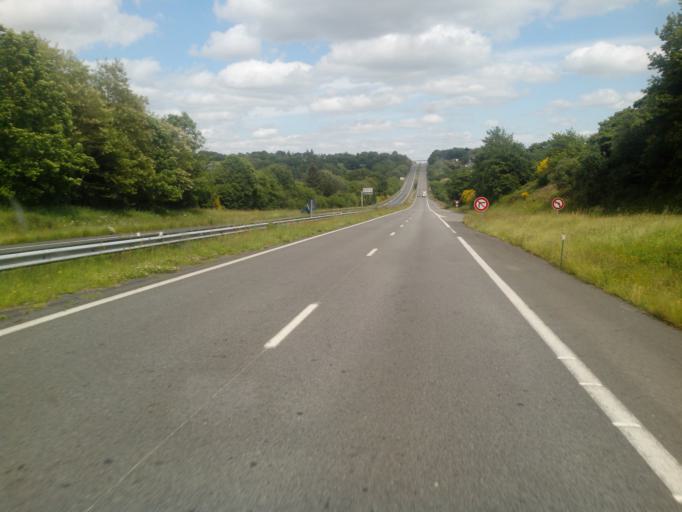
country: FR
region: Brittany
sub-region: Departement des Cotes-d'Armor
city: Belle-Isle-en-Terre
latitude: 48.5496
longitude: -3.4045
